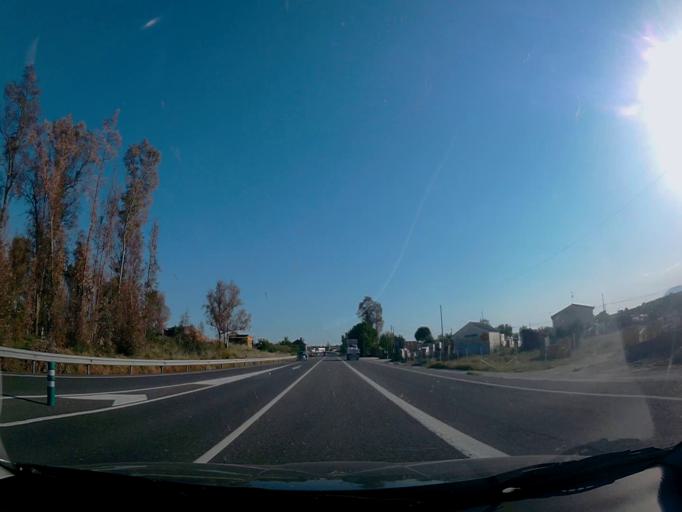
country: ES
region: Castille-La Mancha
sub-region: Province of Toledo
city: Escalona
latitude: 40.1563
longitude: -4.4010
